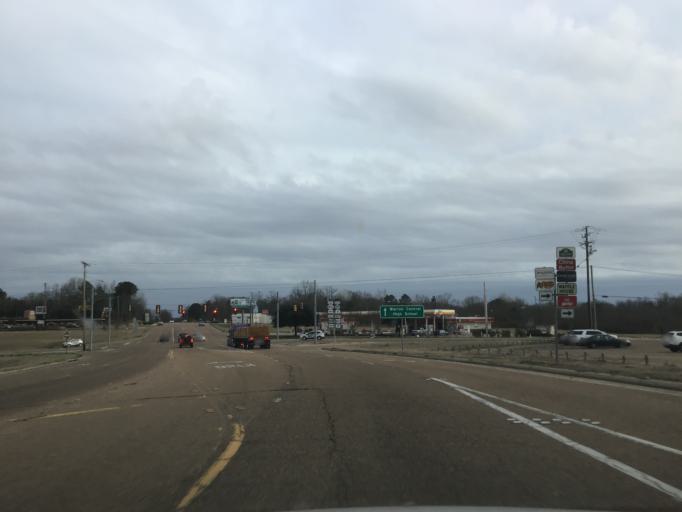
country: US
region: Mississippi
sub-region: Warren County
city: Beechwood
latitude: 32.3453
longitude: -90.8296
